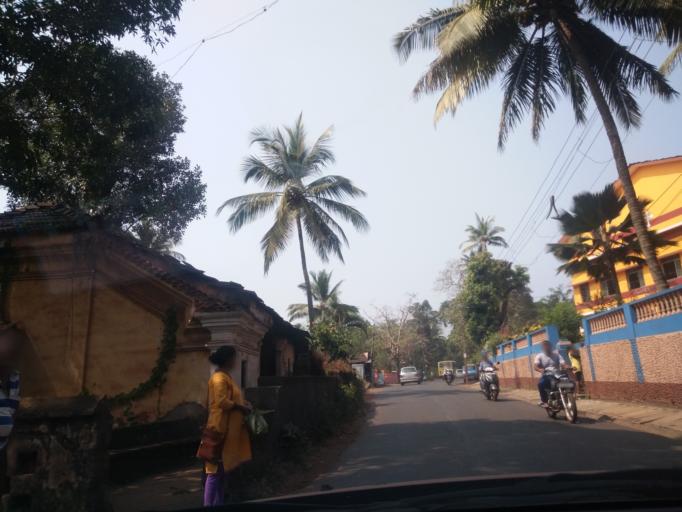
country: IN
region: Goa
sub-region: North Goa
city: Aldona
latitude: 15.6196
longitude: 73.8944
